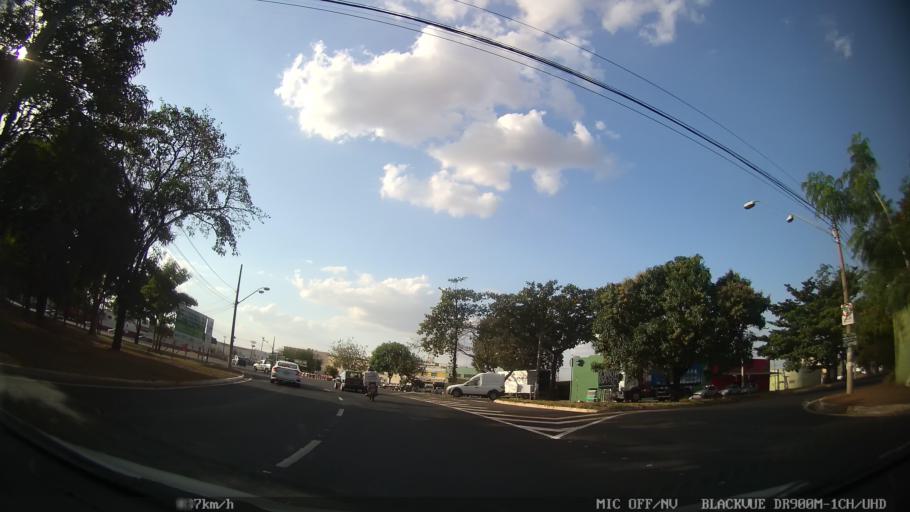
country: BR
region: Sao Paulo
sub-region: Ribeirao Preto
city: Ribeirao Preto
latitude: -21.1382
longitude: -47.7971
